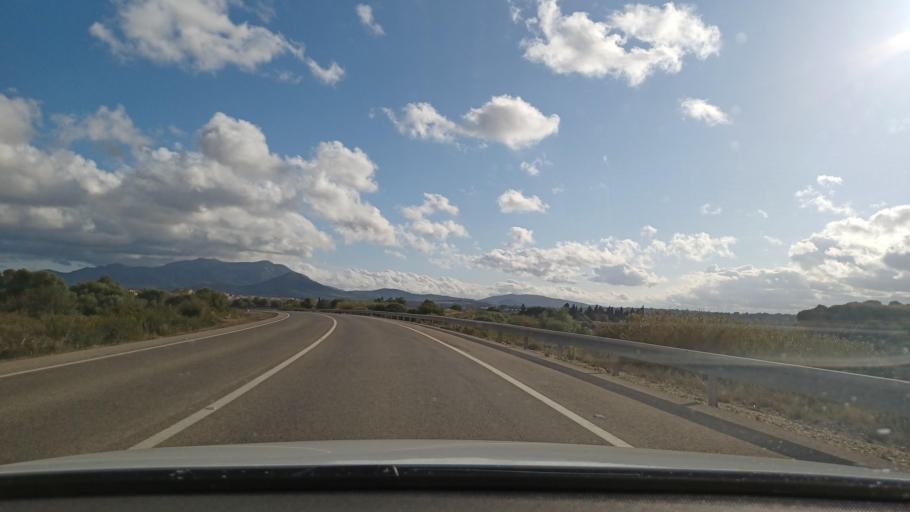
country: ES
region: Catalonia
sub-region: Provincia de Tarragona
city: Amposta
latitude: 40.7341
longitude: 0.5859
